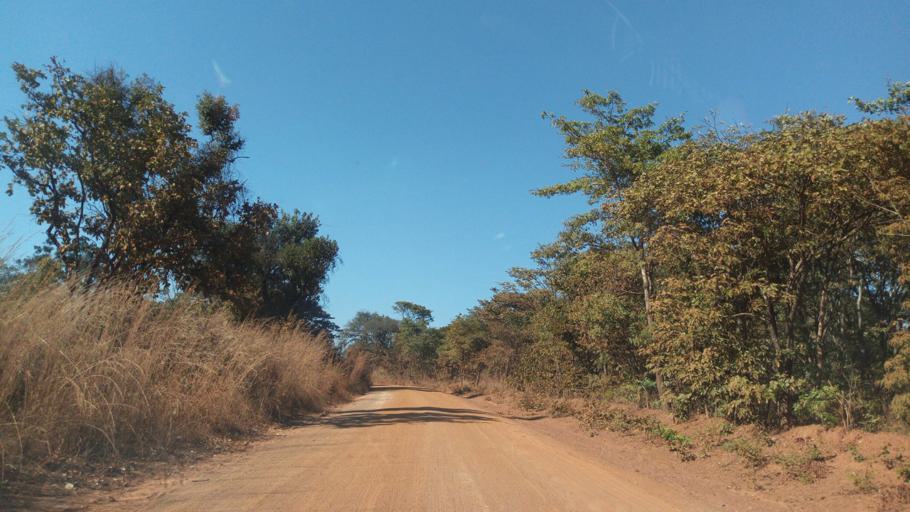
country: ZM
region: Luapula
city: Mwense
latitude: -10.6639
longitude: 28.4085
